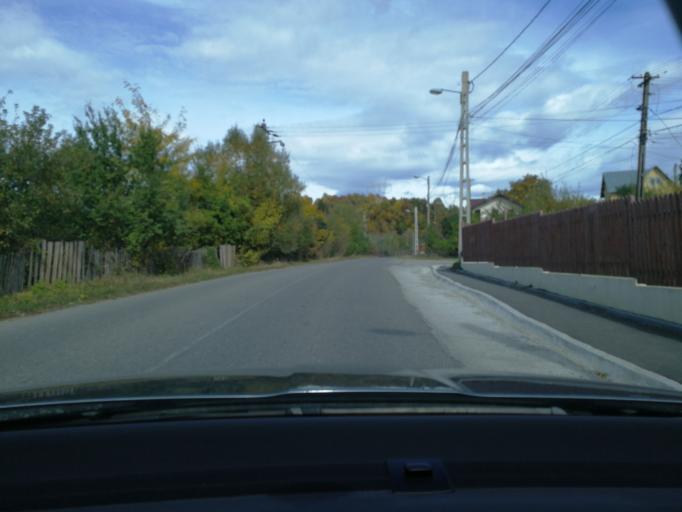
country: RO
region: Prahova
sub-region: Comuna Telega
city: Telega
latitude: 45.1453
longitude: 25.7707
